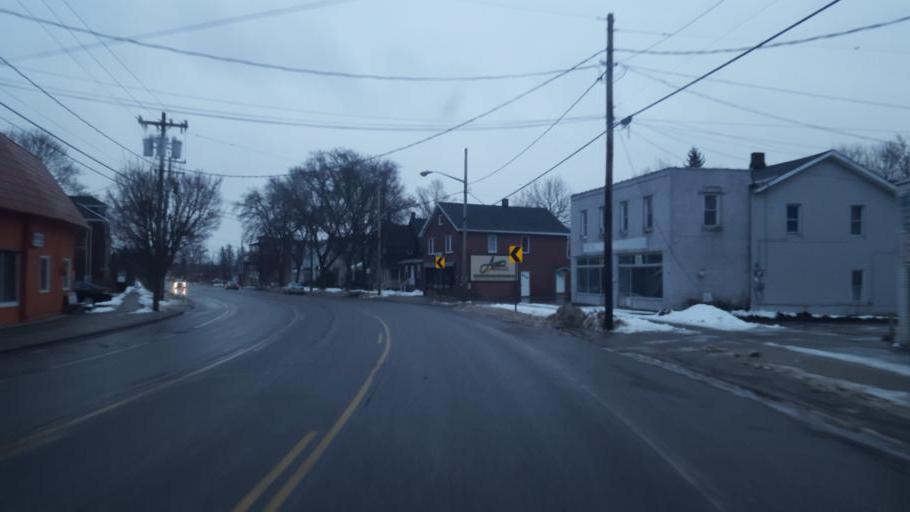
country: US
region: New York
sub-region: Chautauqua County
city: Falconer
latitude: 42.1143
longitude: -79.2033
